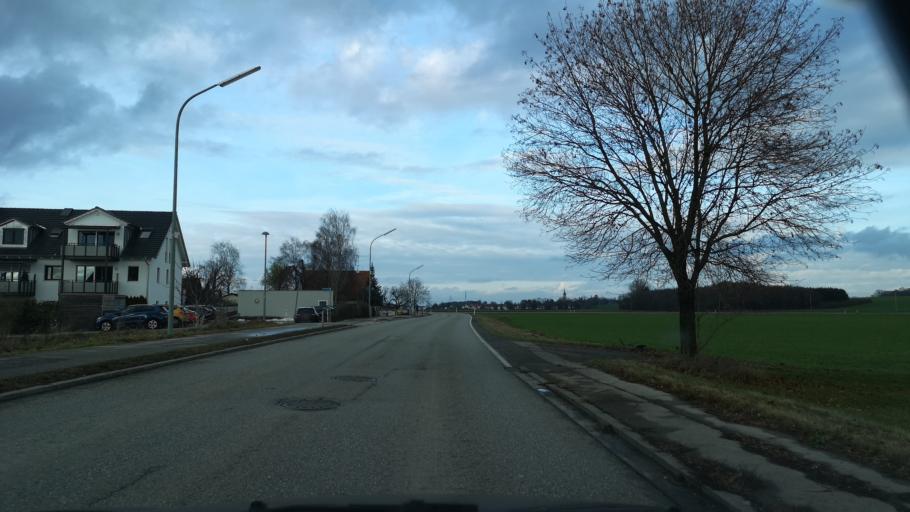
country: DE
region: Bavaria
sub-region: Upper Bavaria
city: Pliening
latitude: 48.1837
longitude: 11.8078
